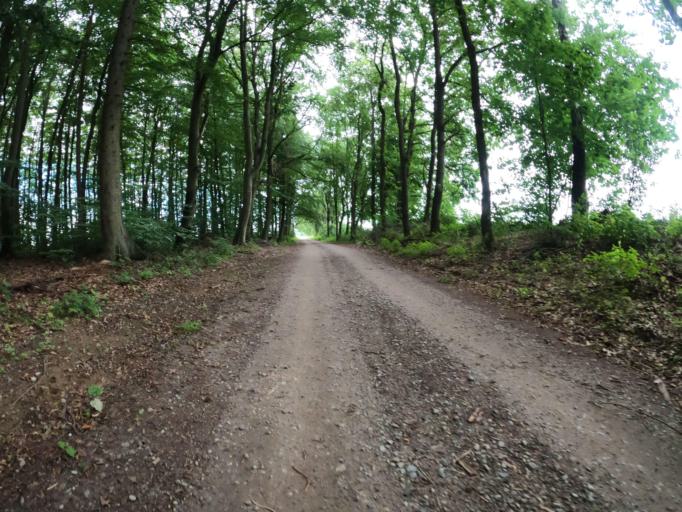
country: PL
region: West Pomeranian Voivodeship
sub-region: Powiat bialogardzki
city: Tychowo
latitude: 53.9932
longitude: 16.3805
